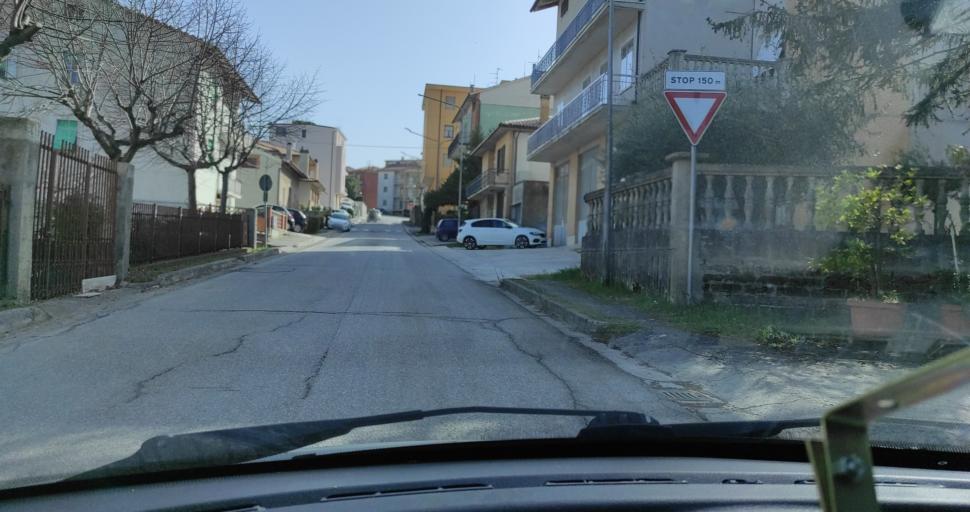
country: IT
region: The Marches
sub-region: Provincia di Macerata
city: Loro Piceno
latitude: 43.1646
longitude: 13.4084
